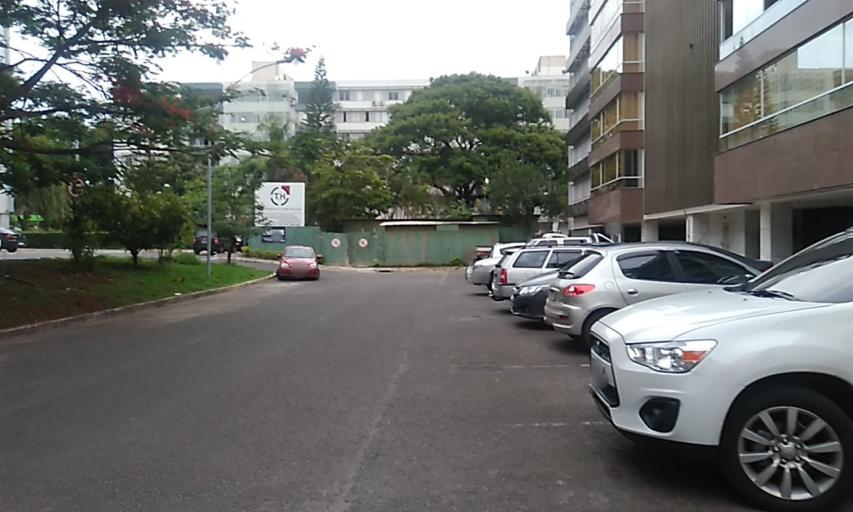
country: BR
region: Federal District
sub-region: Brasilia
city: Brasilia
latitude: -15.7760
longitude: -47.8868
